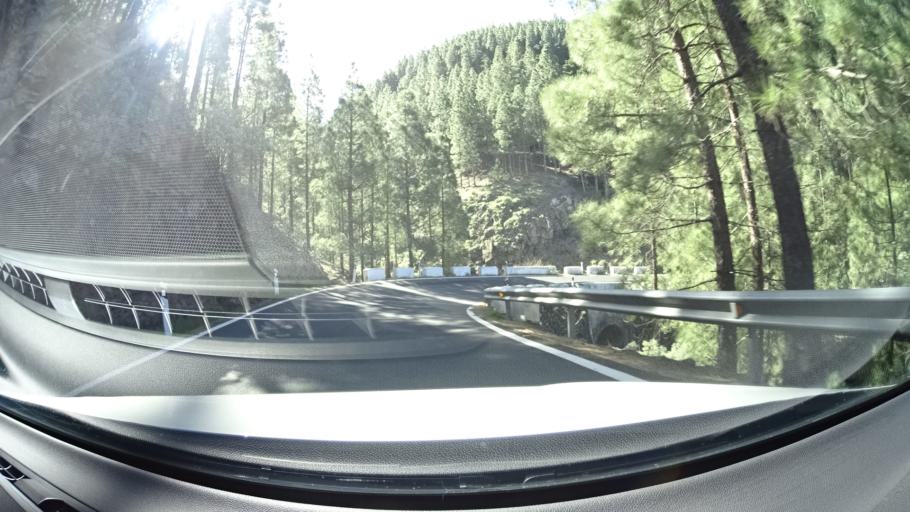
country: ES
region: Canary Islands
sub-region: Provincia de Las Palmas
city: Artenara
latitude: 28.0233
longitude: -15.6231
